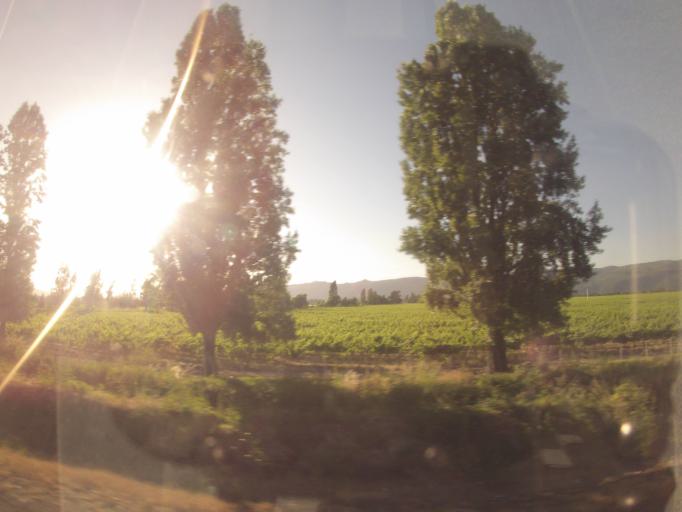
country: CL
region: O'Higgins
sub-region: Provincia de Colchagua
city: Chimbarongo
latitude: -34.7398
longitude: -71.0410
